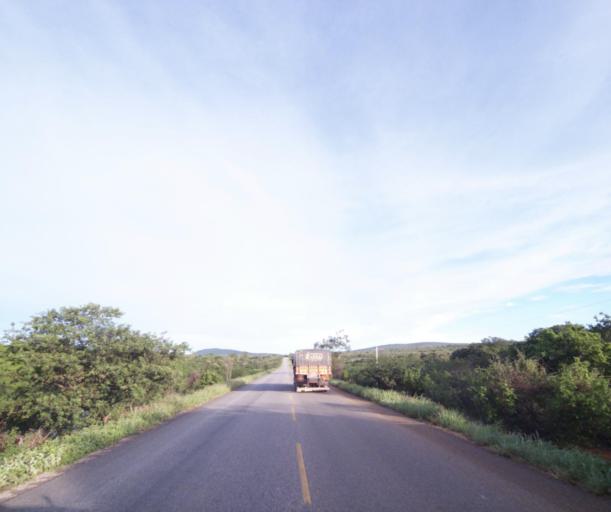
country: BR
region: Bahia
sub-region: Caetite
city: Caetite
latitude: -14.1741
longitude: -42.1822
